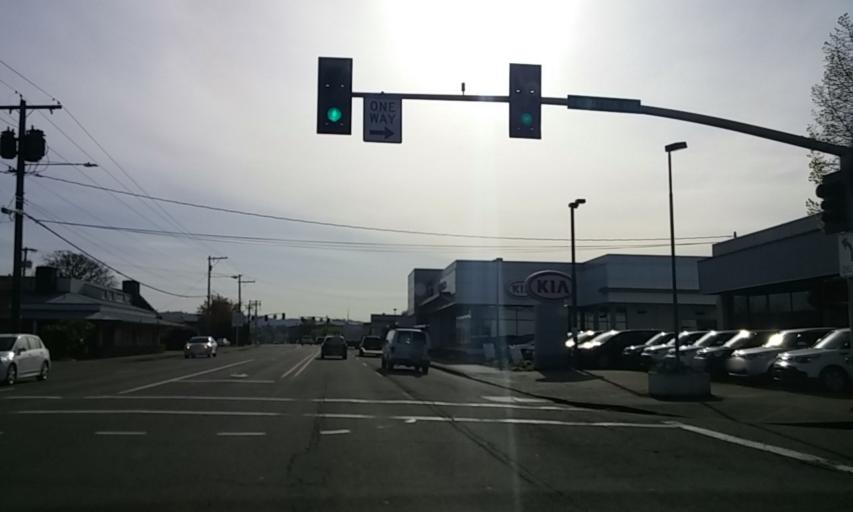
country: US
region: Oregon
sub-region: Washington County
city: Beaverton
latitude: 45.4883
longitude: -122.8066
